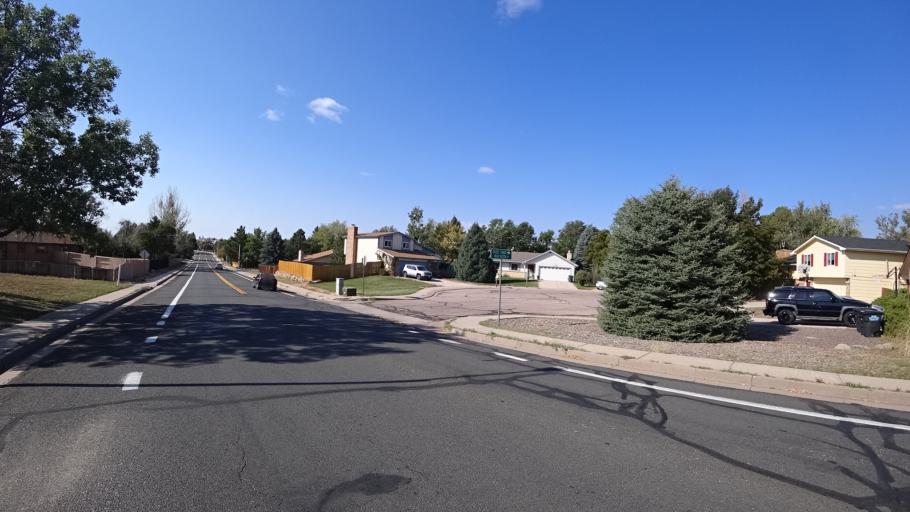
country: US
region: Colorado
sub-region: El Paso County
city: Cimarron Hills
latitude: 38.8819
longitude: -104.7224
